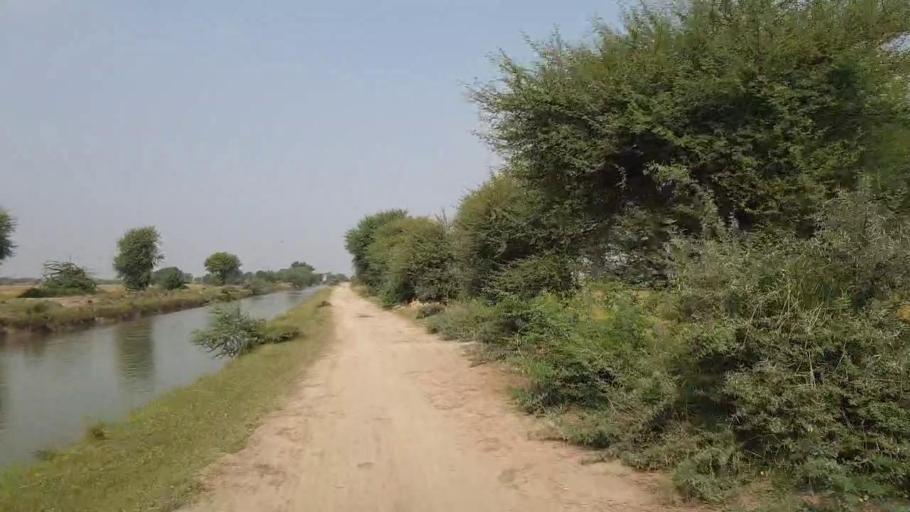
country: PK
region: Sindh
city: Kario
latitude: 24.8426
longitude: 68.5376
